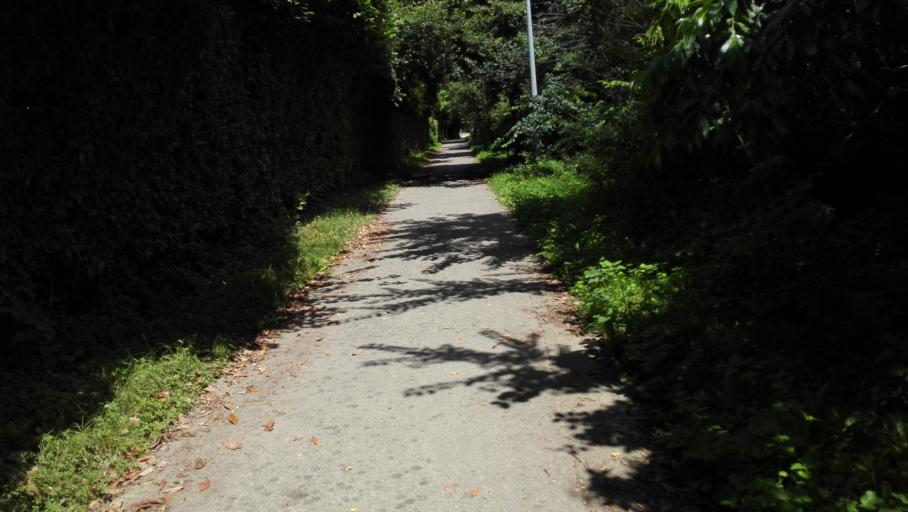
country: BE
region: Flanders
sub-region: Provincie Vlaams-Brabant
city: Tienen
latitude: 50.8031
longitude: 4.9706
